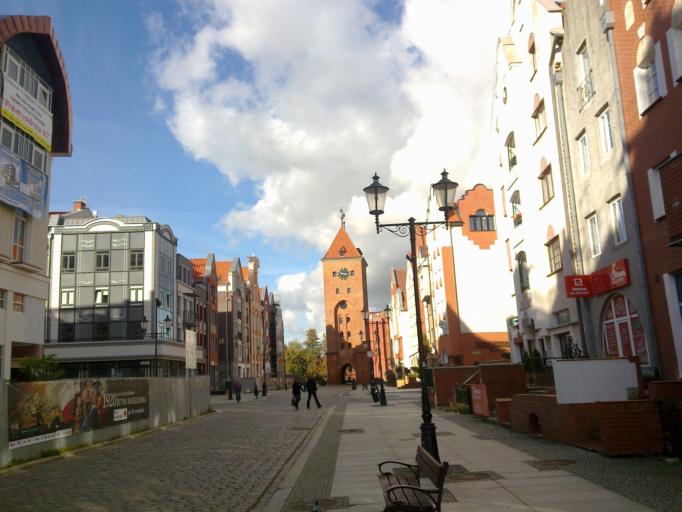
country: PL
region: Warmian-Masurian Voivodeship
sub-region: Powiat elblaski
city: Elblag
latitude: 54.1594
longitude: 19.3956
